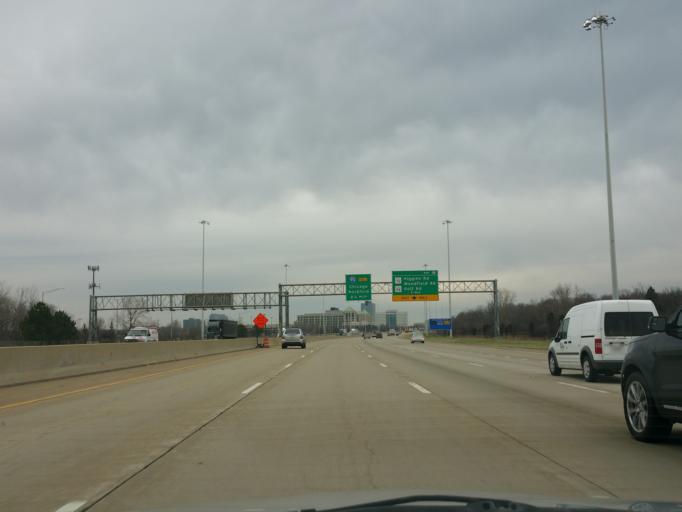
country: US
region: Illinois
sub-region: DuPage County
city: Itasca
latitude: 42.0145
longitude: -88.0303
